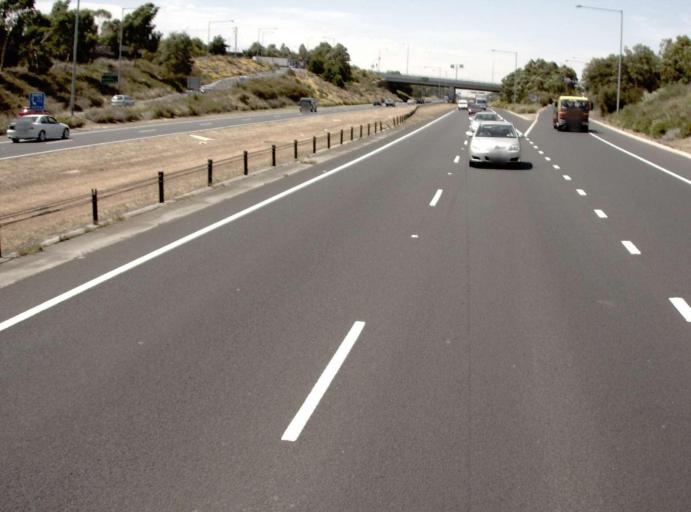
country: AU
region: Victoria
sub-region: Casey
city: Narre Warren
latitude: -38.0151
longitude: 145.3054
